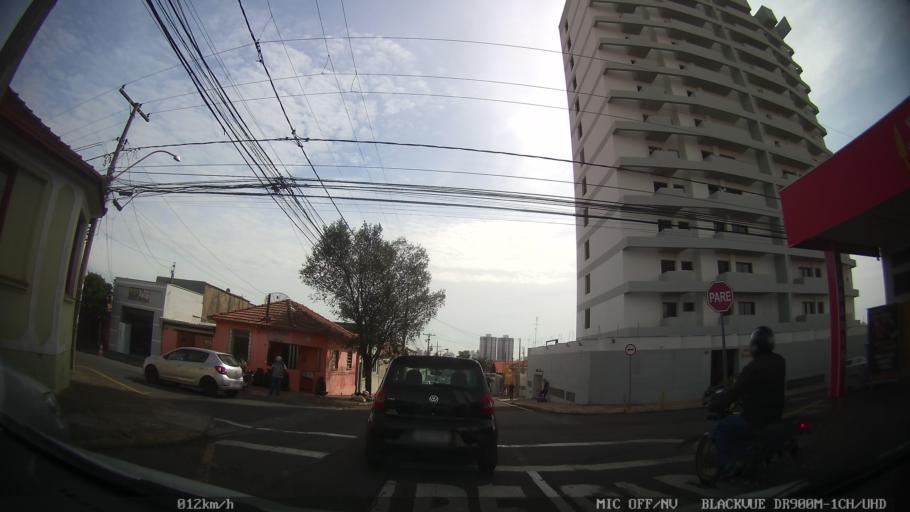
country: BR
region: Sao Paulo
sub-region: Piracicaba
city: Piracicaba
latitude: -22.7488
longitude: -47.6487
